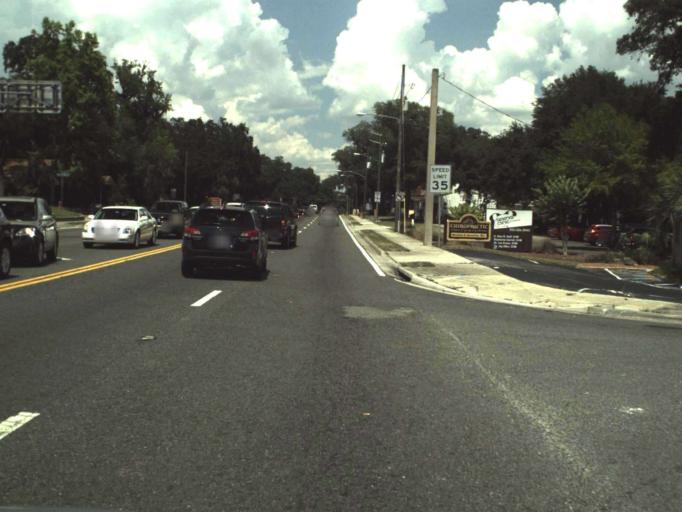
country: US
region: Florida
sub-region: Lake County
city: Leesburg
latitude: 28.8032
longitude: -81.8868
